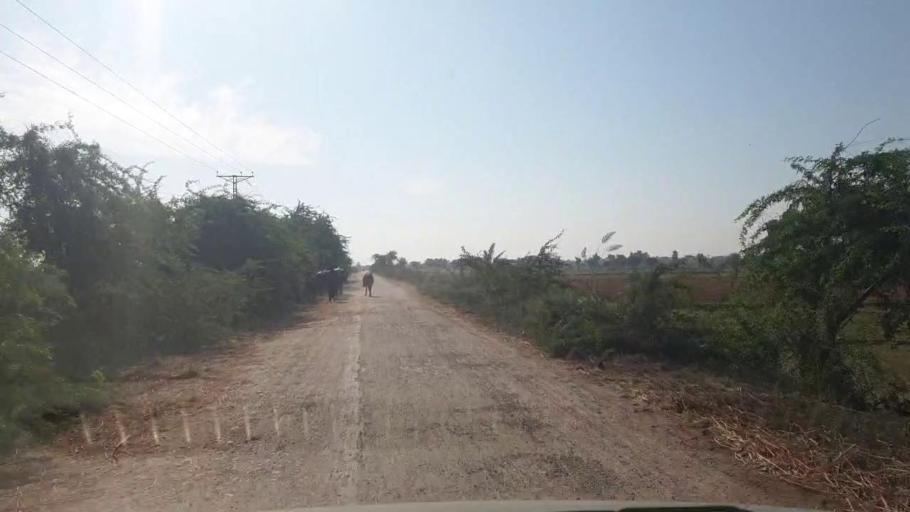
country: PK
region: Sindh
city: Talhar
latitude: 24.9032
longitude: 68.8228
